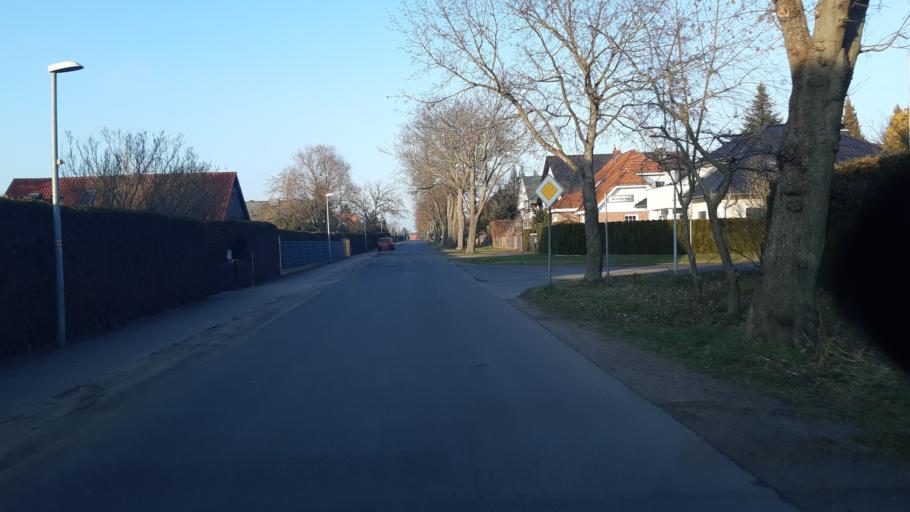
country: DE
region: Brandenburg
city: Velten
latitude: 52.7112
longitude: 13.1483
